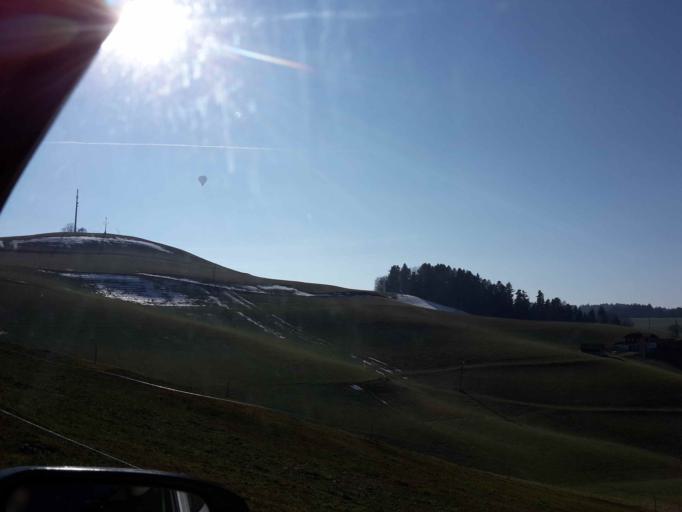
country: CH
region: Bern
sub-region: Emmental District
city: Durrenroth
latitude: 47.1140
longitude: 7.7891
